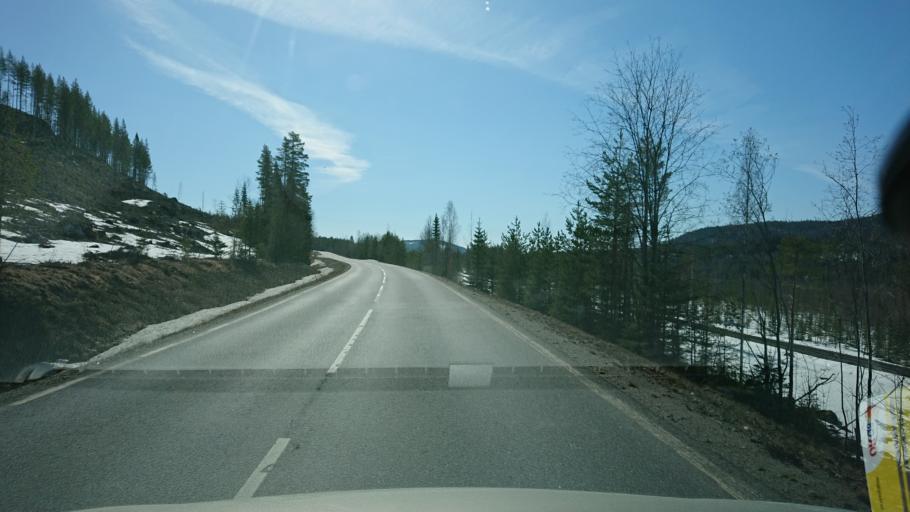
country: SE
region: Vaesterbotten
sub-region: Dorotea Kommun
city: Dorotea
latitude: 64.0387
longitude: 16.2600
